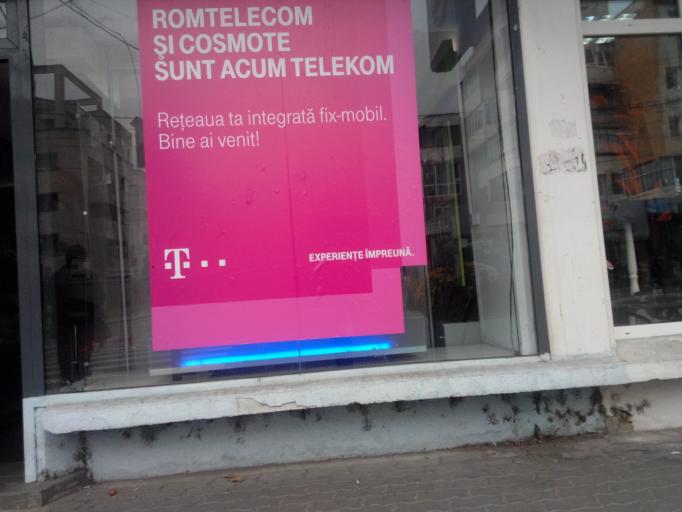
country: RO
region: Vaslui
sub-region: Municipiul Barlad
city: Barlad
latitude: 46.2257
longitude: 27.6699
